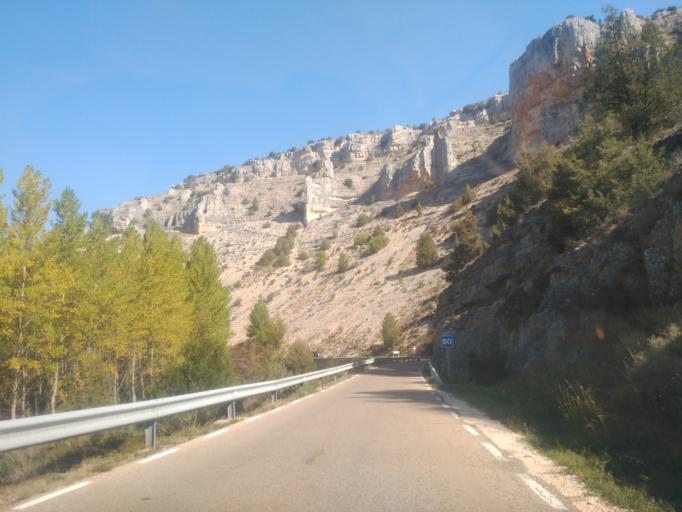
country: ES
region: Castille and Leon
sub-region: Provincia de Soria
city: Ucero
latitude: 41.7312
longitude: -3.0451
